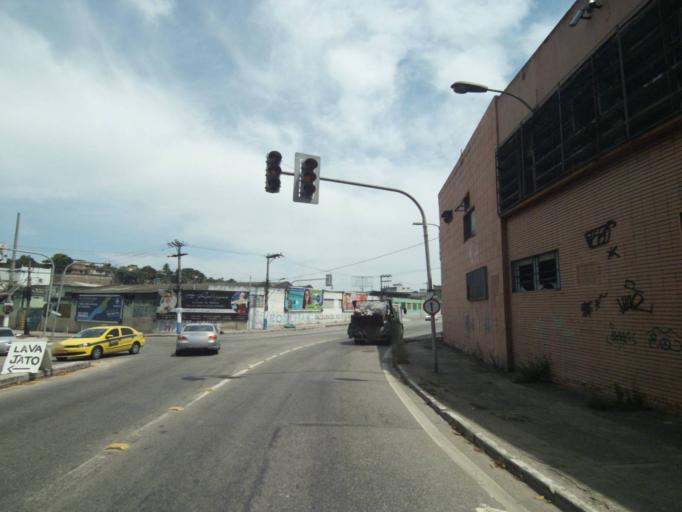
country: BR
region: Rio de Janeiro
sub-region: Sao Joao De Meriti
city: Sao Joao de Meriti
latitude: -22.8008
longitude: -43.3552
